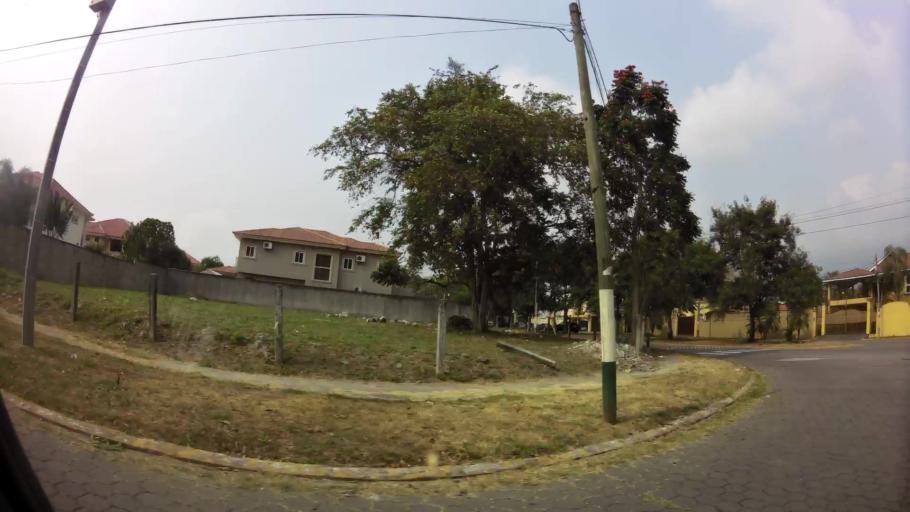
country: HN
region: Cortes
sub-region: San Pedro Sula
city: Pena Blanca
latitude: 15.5376
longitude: -88.0274
